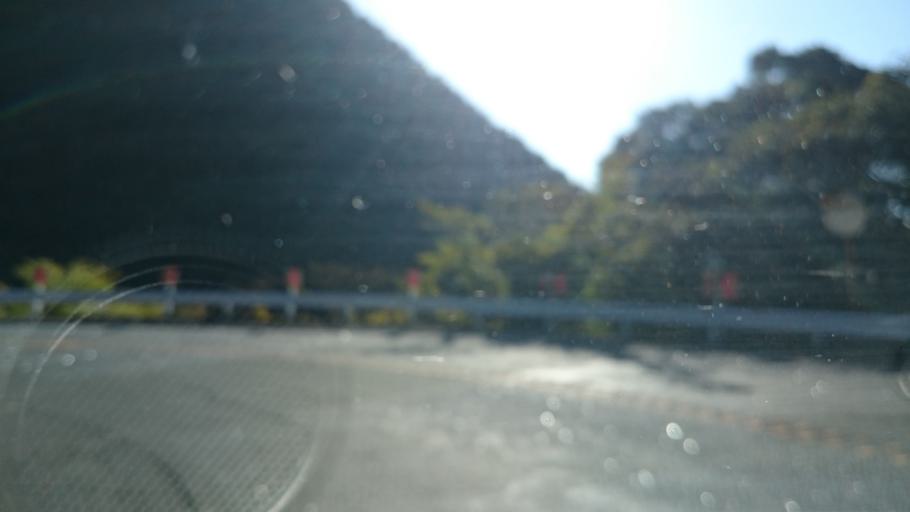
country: JP
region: Shizuoka
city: Heda
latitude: 34.9731
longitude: 138.8161
